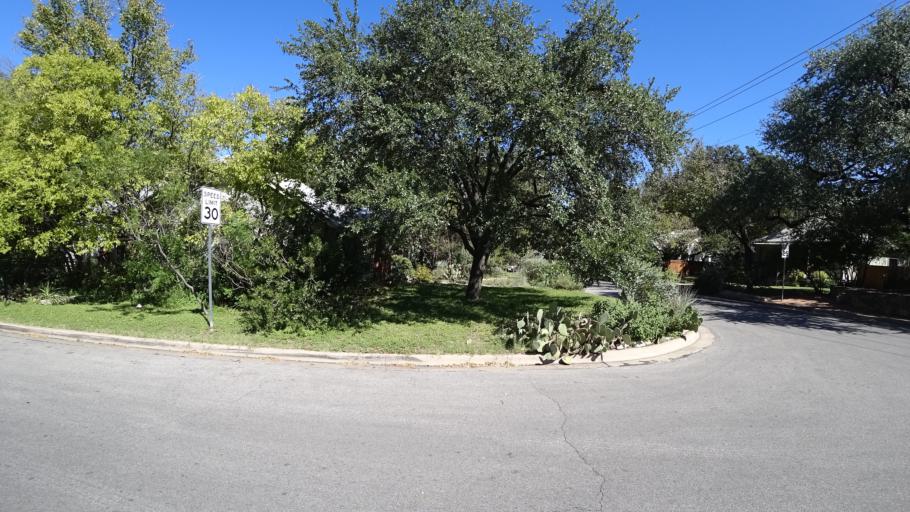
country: US
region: Texas
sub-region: Travis County
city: Austin
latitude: 30.2446
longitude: -97.7492
